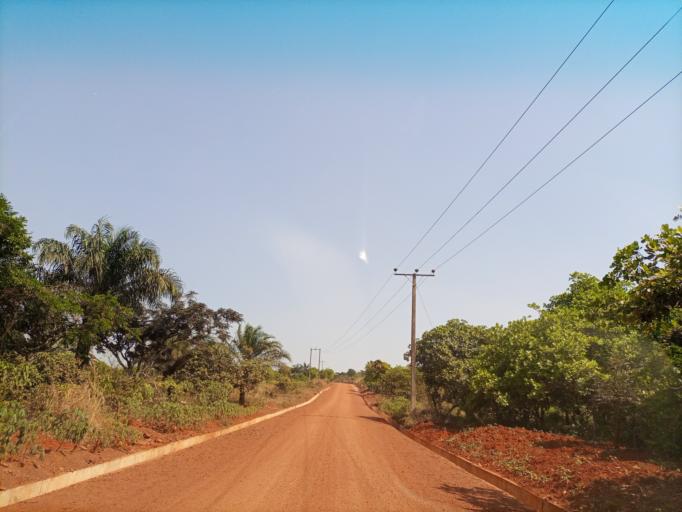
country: NG
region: Enugu
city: Nsukka
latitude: 6.8002
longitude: 7.3423
